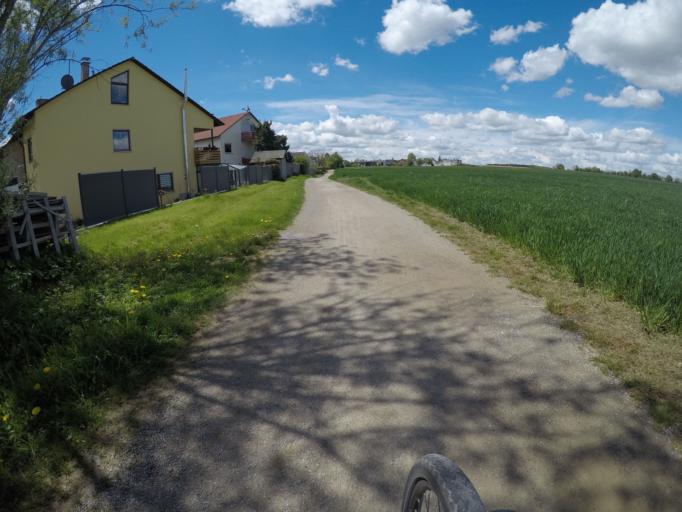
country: DE
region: Baden-Wuerttemberg
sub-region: Regierungsbezirk Stuttgart
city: Altdorf
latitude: 48.6339
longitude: 8.9916
